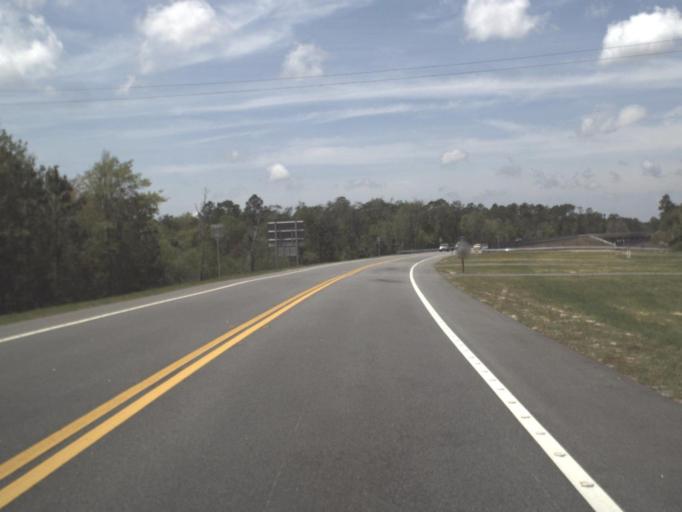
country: US
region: Florida
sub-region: Escambia County
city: Cantonment
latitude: 30.5226
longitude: -87.4408
